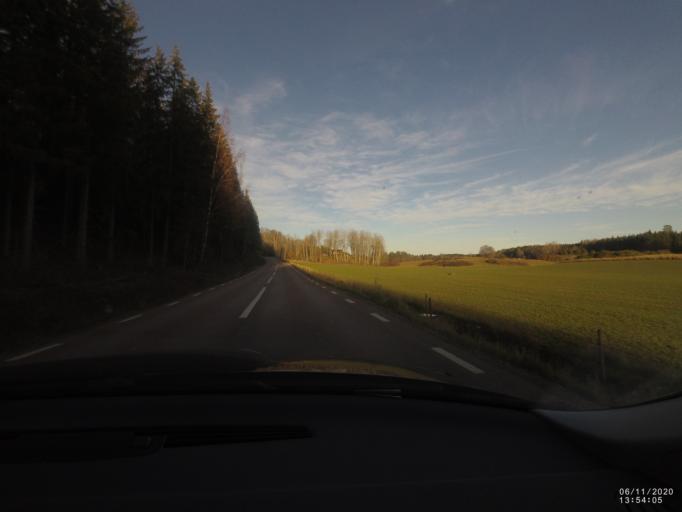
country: SE
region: Soedermanland
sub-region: Gnesta Kommun
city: Gnesta
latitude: 58.9661
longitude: 17.1440
